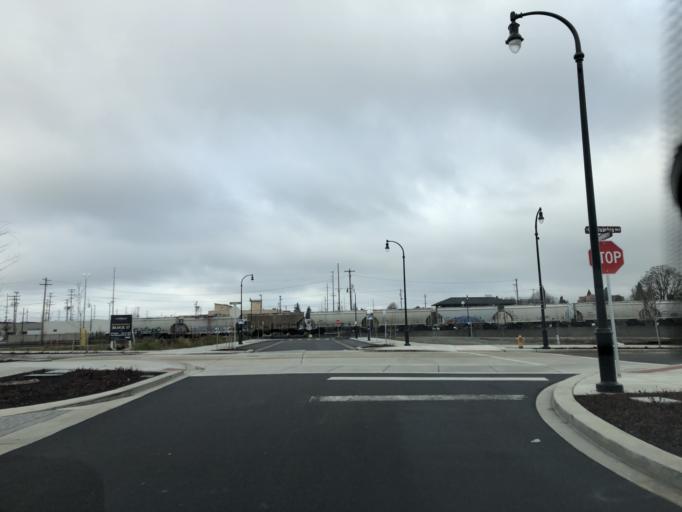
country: US
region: Washington
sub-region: Clark County
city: Vancouver
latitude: 45.6253
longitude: -122.6815
